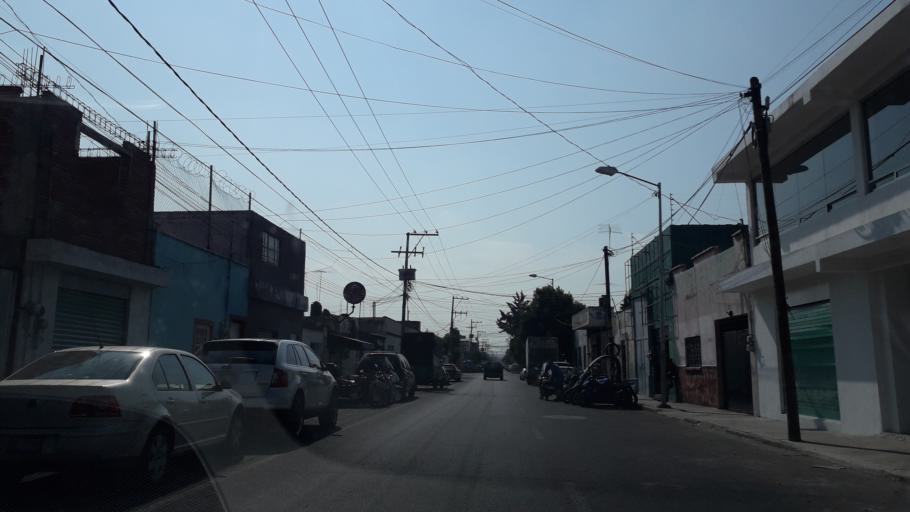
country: MX
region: Puebla
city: Puebla
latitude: 19.0440
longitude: -98.2173
